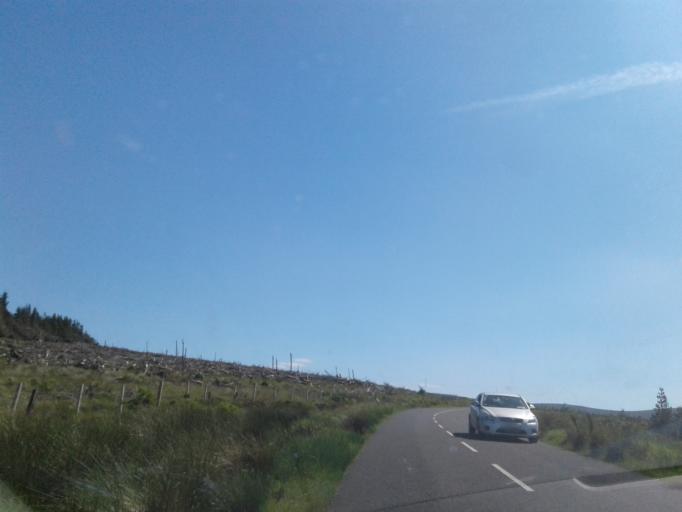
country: IE
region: Leinster
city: Ballyboden
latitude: 53.2350
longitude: -6.3221
